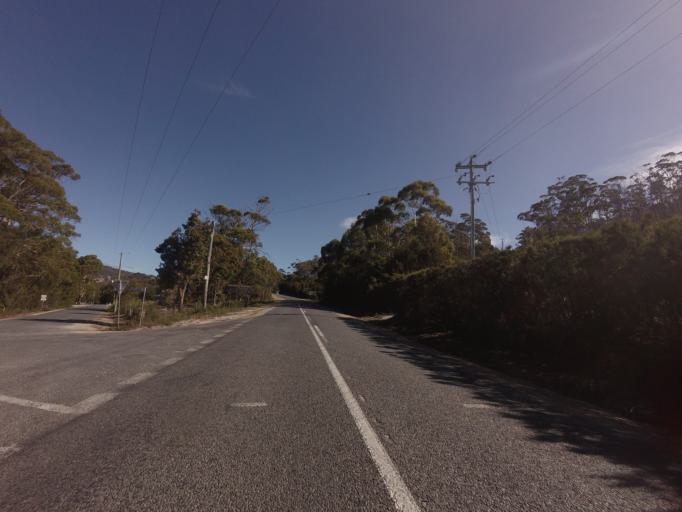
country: AU
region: Tasmania
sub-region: Break O'Day
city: St Helens
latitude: -41.8847
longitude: 148.2995
